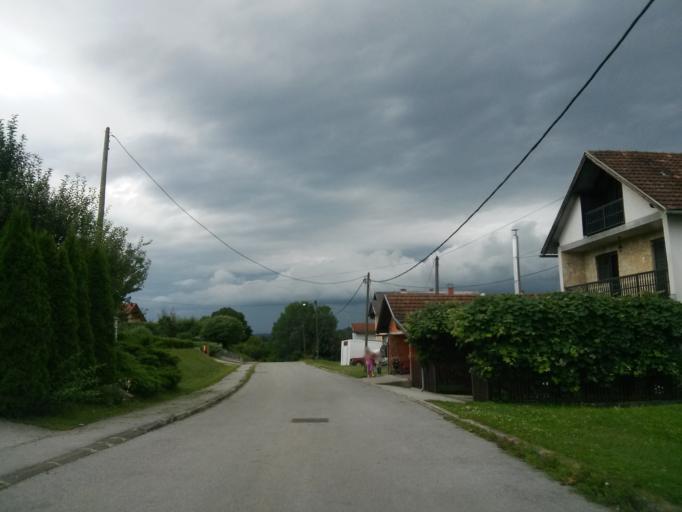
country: HR
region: Sisacko-Moslavacka
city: Gvozd
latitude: 45.3061
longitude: 15.9701
